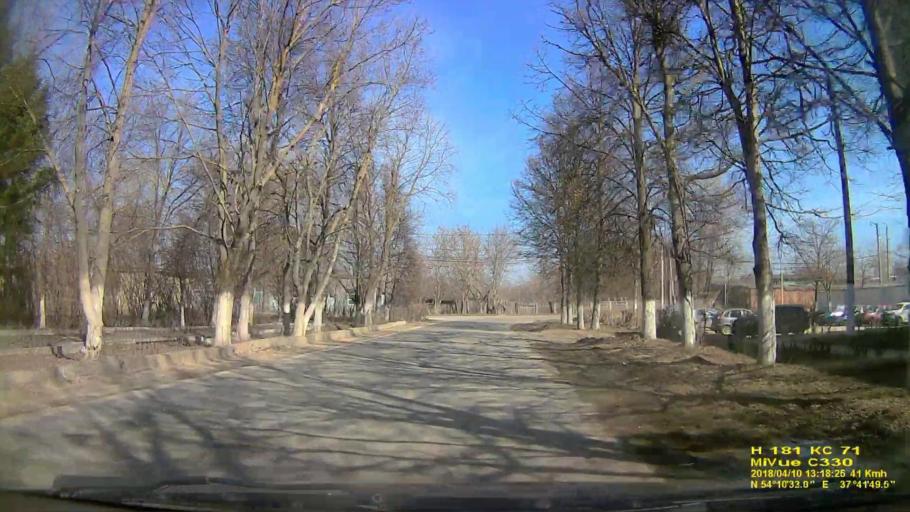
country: RU
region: Tula
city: Tula
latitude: 54.1758
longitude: 37.6971
